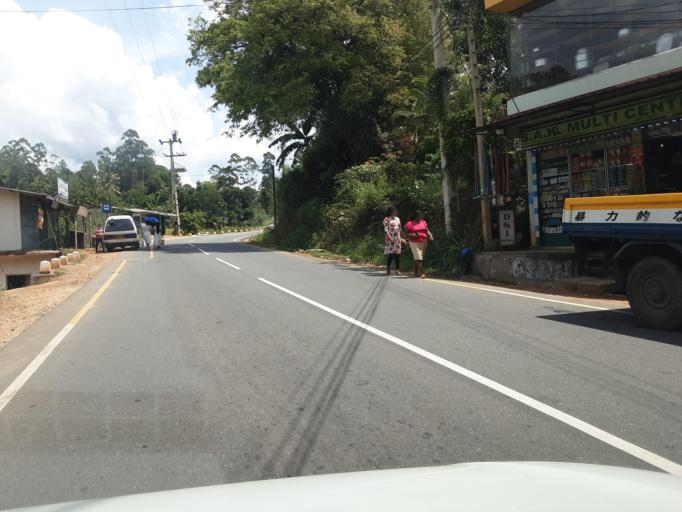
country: LK
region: Central
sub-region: Nuwara Eliya District
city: Nuwara Eliya
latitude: 6.9200
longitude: 80.9016
